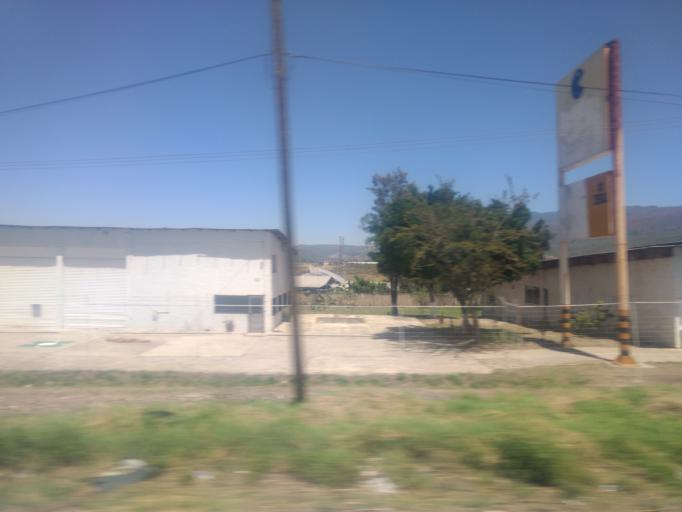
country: MX
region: Jalisco
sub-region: Acatlan de Juarez
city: Villa de los Ninos
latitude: 20.4419
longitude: -103.5239
